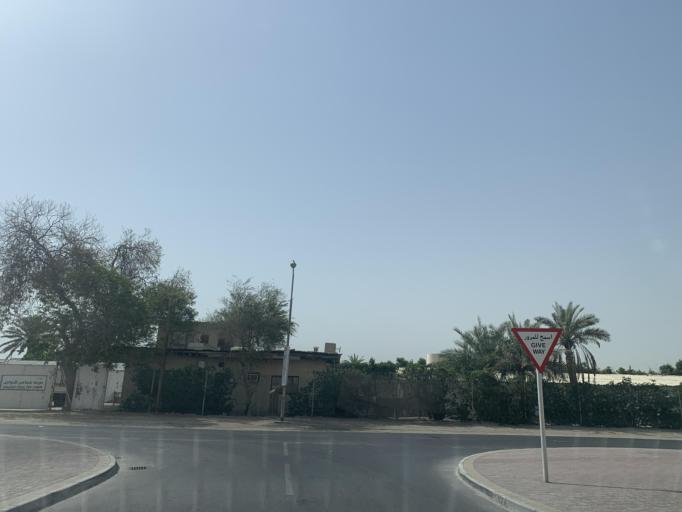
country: BH
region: Northern
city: Madinat `Isa
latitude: 26.1842
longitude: 50.5604
